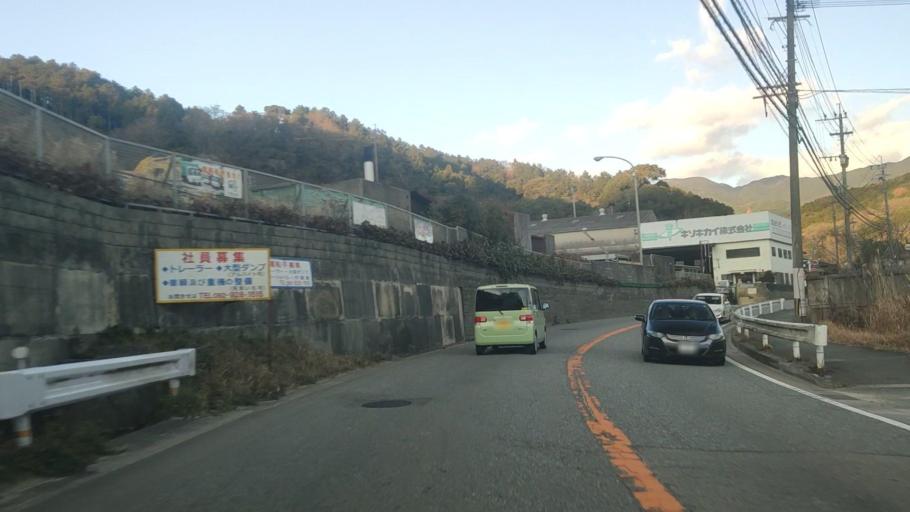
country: JP
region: Fukuoka
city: Dazaifu
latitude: 33.5445
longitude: 130.5391
